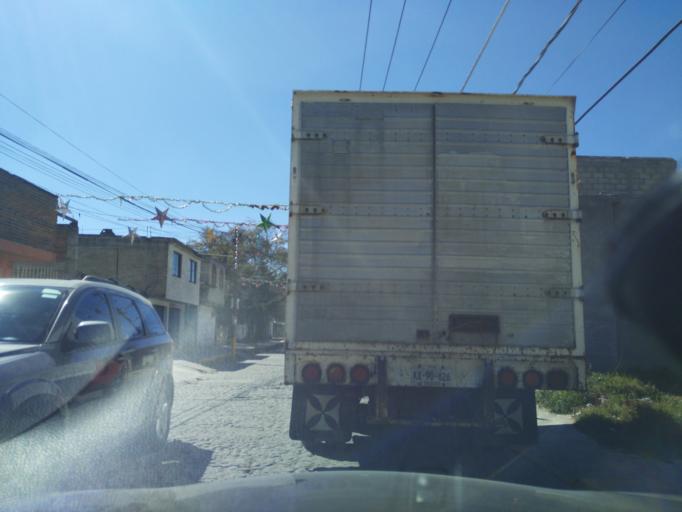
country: MX
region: Morelos
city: Ocoyoacac
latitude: 19.2678
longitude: -99.4630
